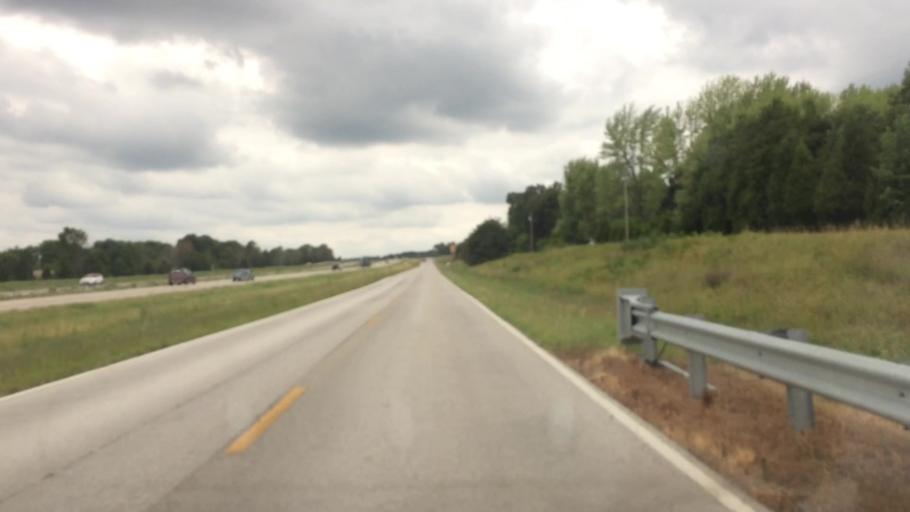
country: US
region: Missouri
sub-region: Greene County
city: Strafford
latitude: 37.2887
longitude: -93.0336
